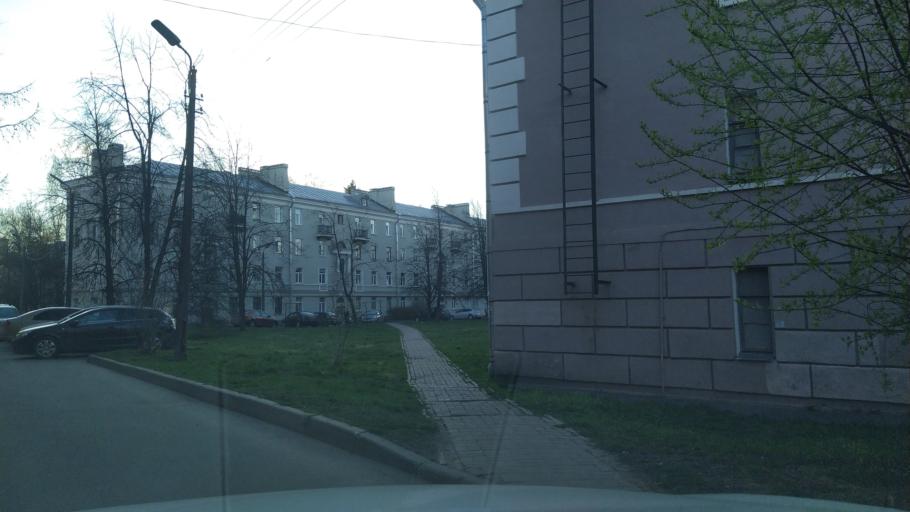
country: RU
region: St.-Petersburg
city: Pushkin
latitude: 59.7043
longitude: 30.3676
